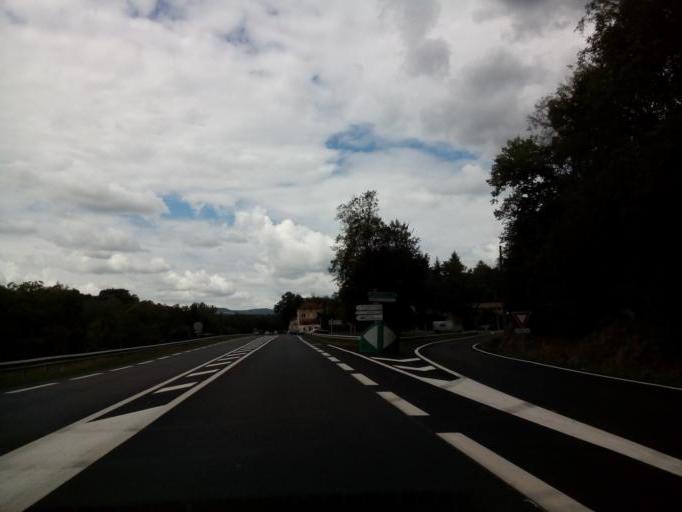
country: FR
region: Rhone-Alpes
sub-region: Departement du Rhone
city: Chatillon
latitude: 45.9012
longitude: 4.5853
